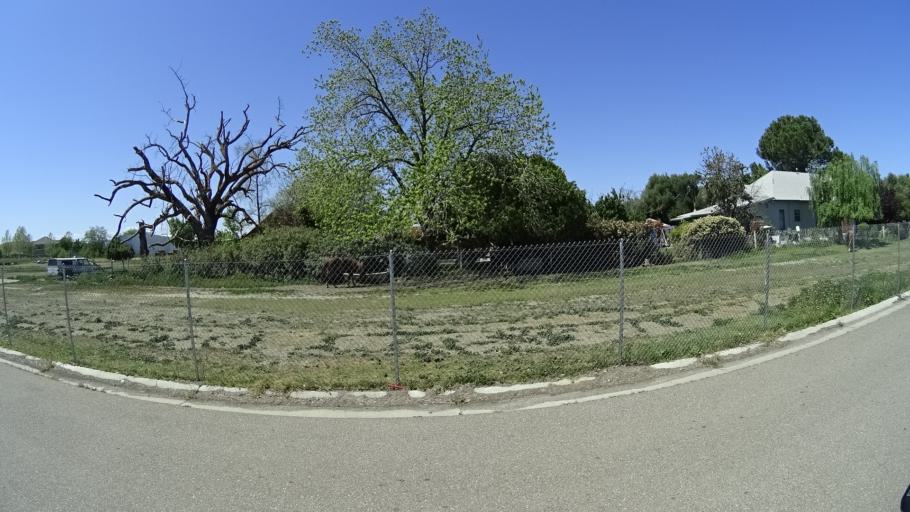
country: US
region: California
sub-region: Glenn County
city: Orland
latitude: 39.7465
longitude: -122.1725
